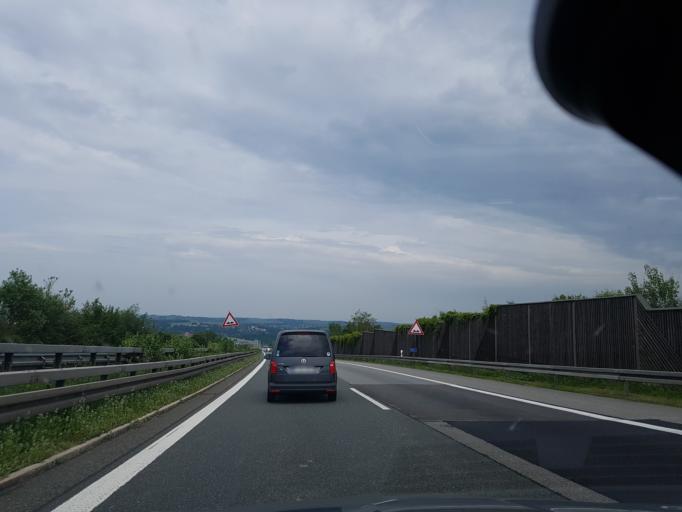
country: DE
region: Saxony
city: Wilkau-Hasslau
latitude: 50.6529
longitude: 12.4988
